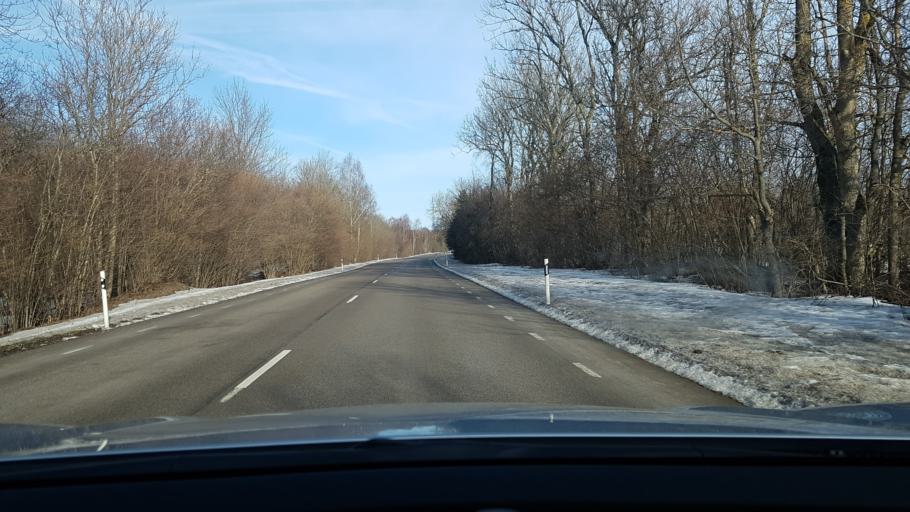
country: EE
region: Saare
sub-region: Orissaare vald
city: Orissaare
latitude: 58.5387
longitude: 23.0498
